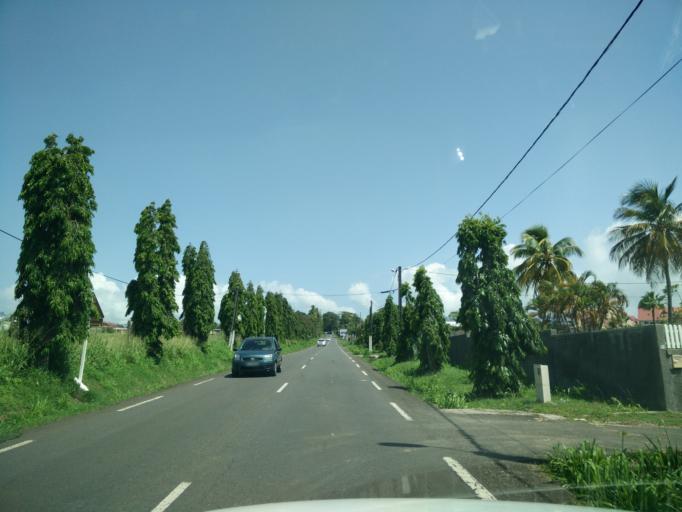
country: GP
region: Guadeloupe
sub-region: Guadeloupe
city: Petit-Bourg
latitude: 16.1802
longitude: -61.5876
